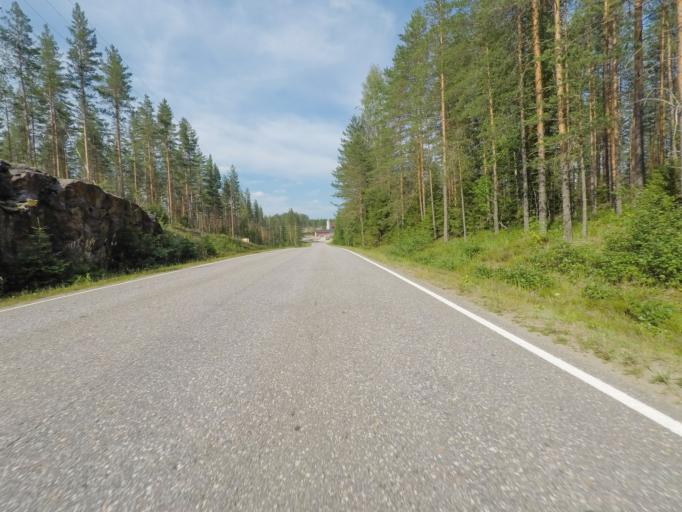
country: FI
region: Southern Savonia
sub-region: Savonlinna
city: Sulkava
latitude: 61.7843
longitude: 28.2413
